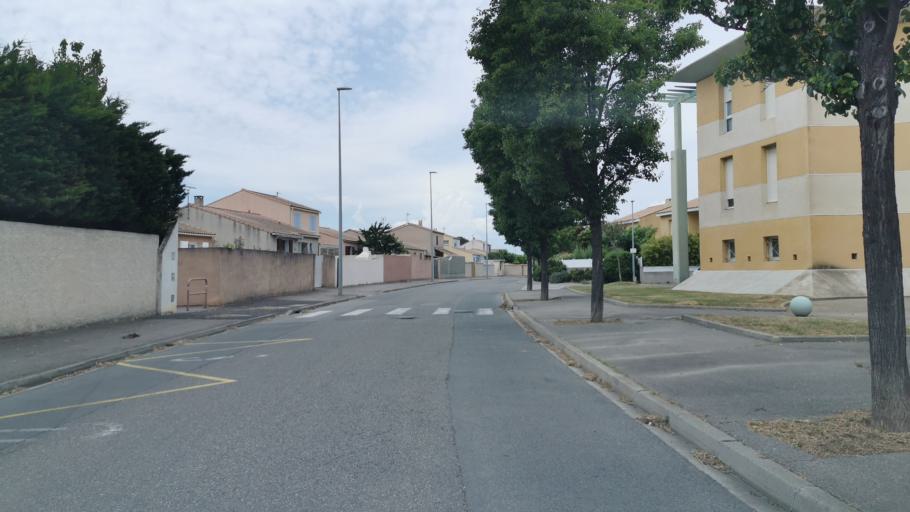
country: FR
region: Languedoc-Roussillon
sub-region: Departement de l'Aude
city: Narbonne
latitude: 43.1937
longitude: 3.0235
